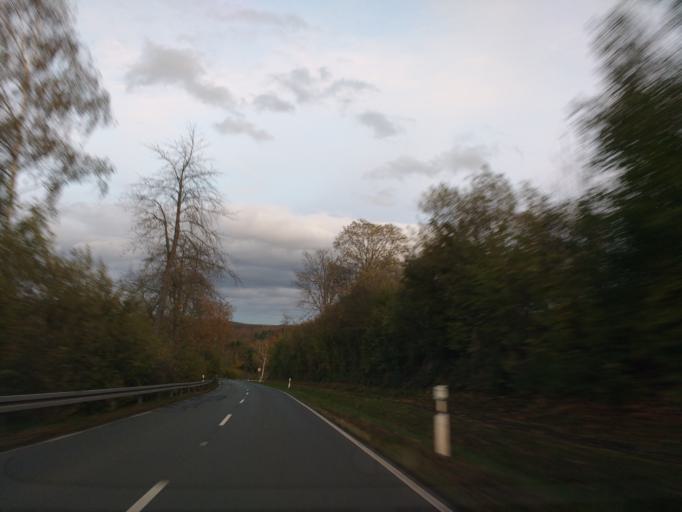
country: DE
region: Hesse
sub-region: Regierungsbezirk Kassel
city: Waldeck
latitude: 51.2042
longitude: 9.0773
